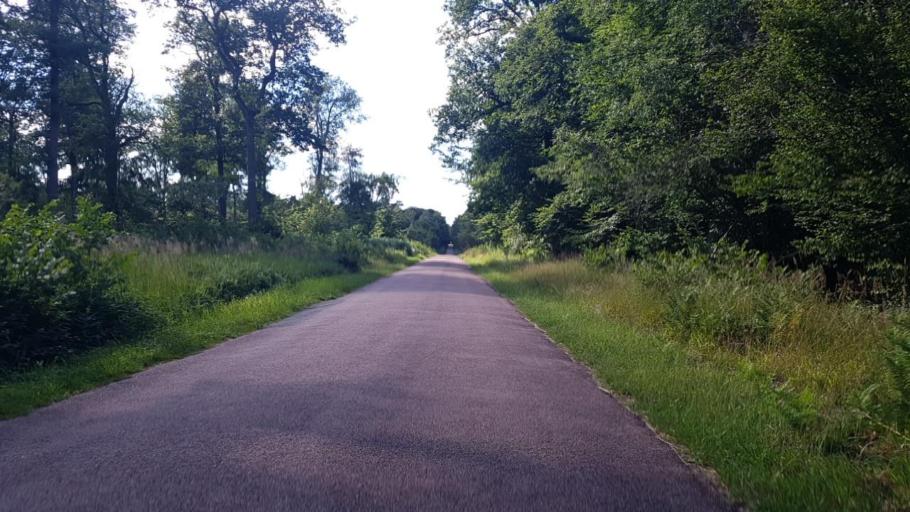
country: FR
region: Picardie
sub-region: Departement de l'Oise
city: Ver-sur-Launette
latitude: 49.1462
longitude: 2.6471
